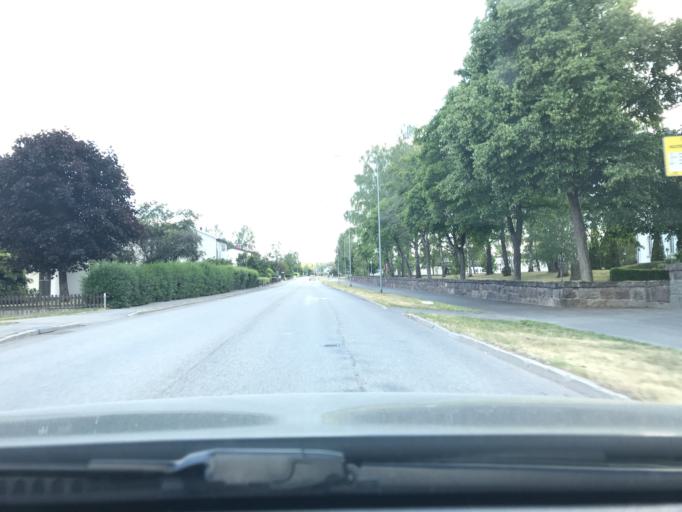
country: SE
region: Kalmar
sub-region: Hultsfreds Kommun
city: Hultsfred
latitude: 57.4956
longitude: 15.8487
